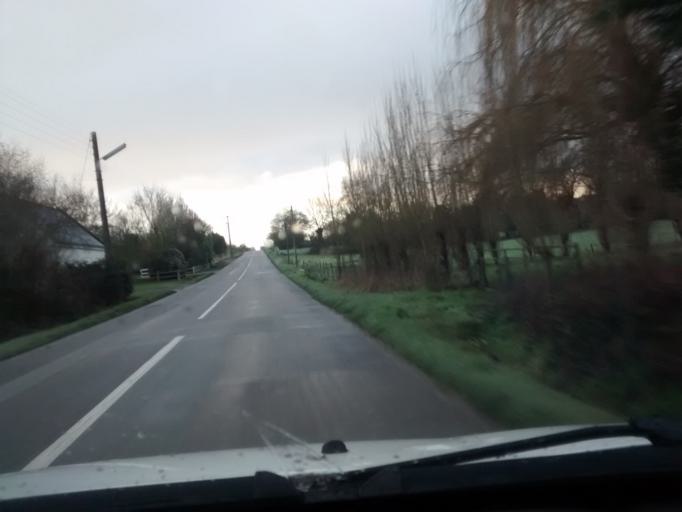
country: FR
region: Brittany
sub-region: Departement d'Ille-et-Vilaine
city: Bais
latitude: 48.0027
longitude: -1.2885
